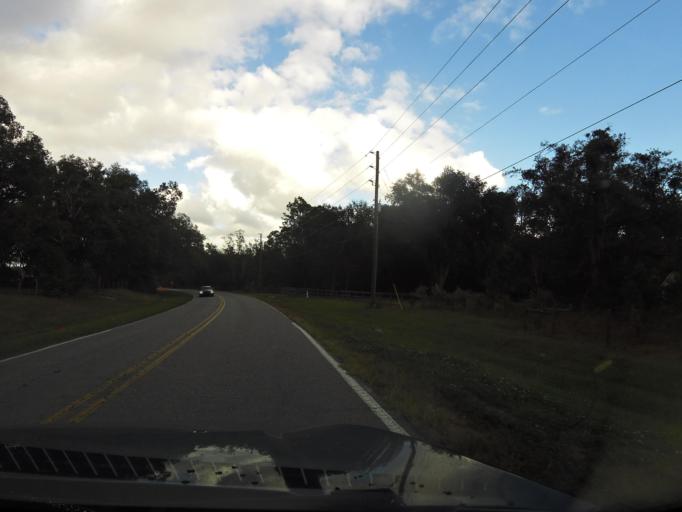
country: US
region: Florida
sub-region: Clay County
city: Asbury Lake
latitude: 30.0486
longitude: -81.7682
